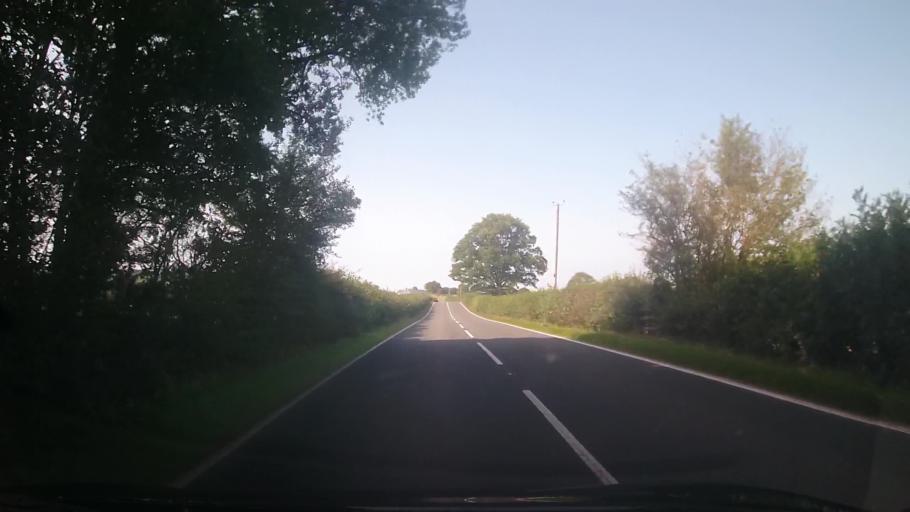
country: GB
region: Wales
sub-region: Sir Powys
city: Builth Wells
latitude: 52.1494
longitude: -3.4223
